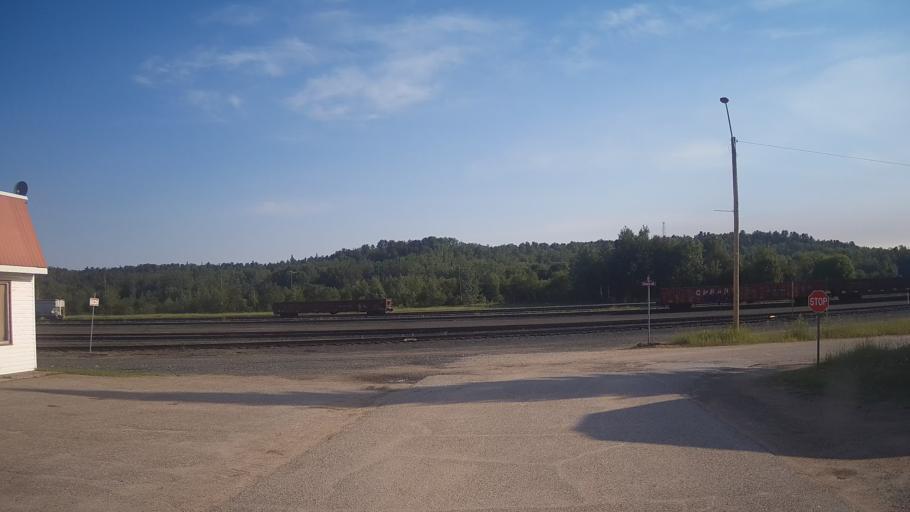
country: CA
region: Ontario
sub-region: Rainy River District
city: Atikokan
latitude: 49.4193
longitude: -91.6680
